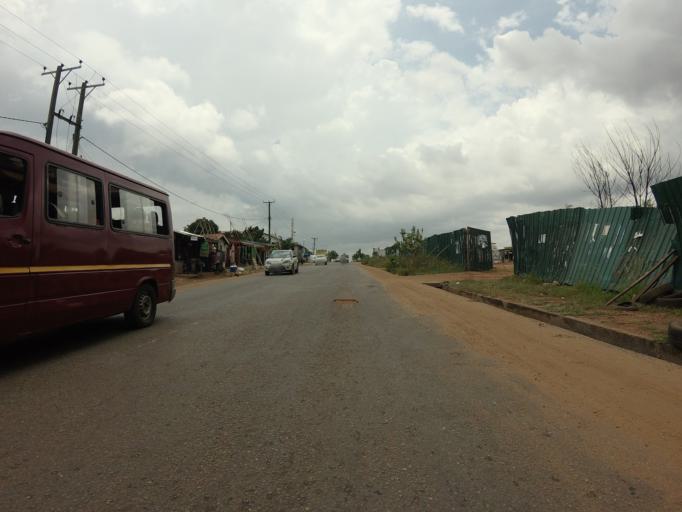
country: GH
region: Greater Accra
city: Medina Estates
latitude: 5.6862
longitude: -0.1589
